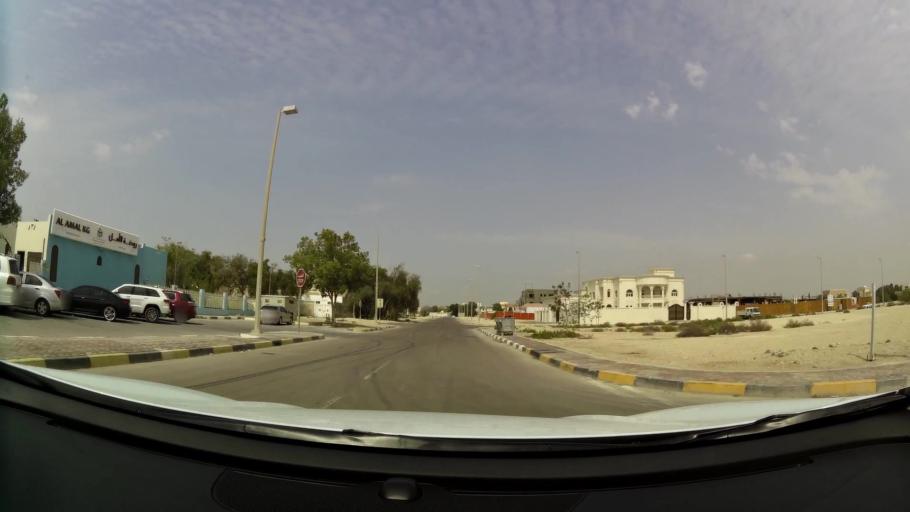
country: AE
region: Abu Dhabi
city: Abu Dhabi
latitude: 24.5248
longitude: 54.6852
